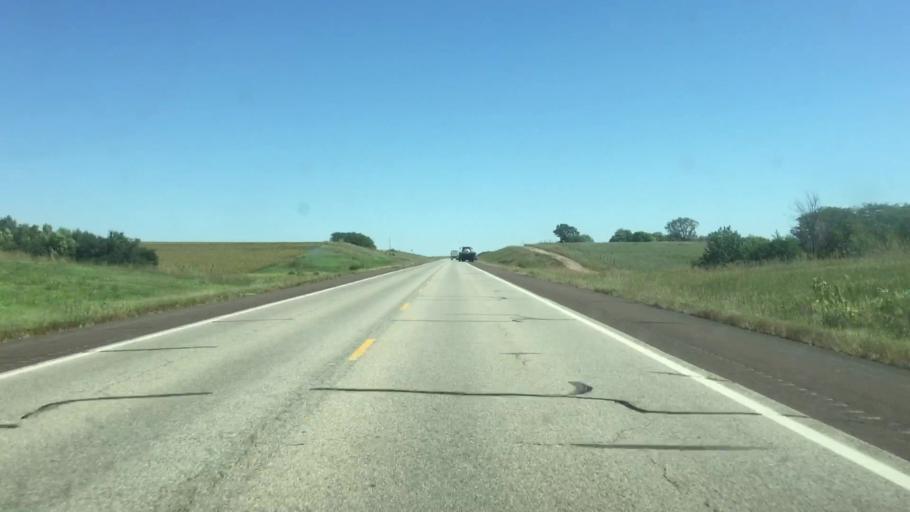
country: US
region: Kansas
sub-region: Nemaha County
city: Seneca
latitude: 39.8421
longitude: -96.2844
